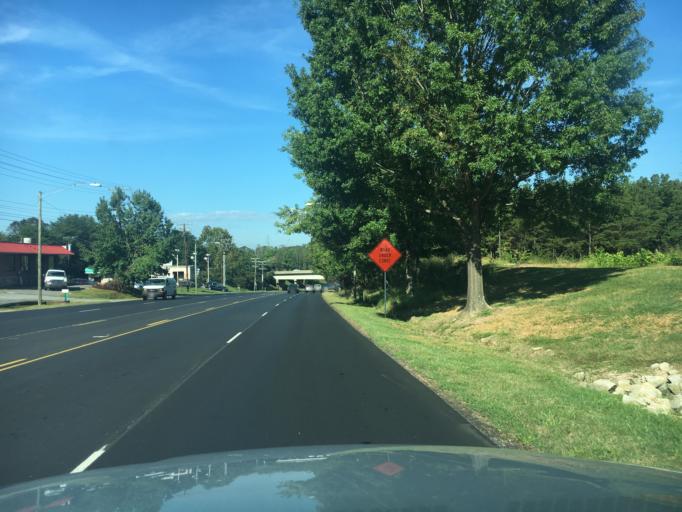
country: US
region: North Carolina
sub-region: Catawba County
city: Hickory
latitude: 35.7119
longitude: -81.3271
